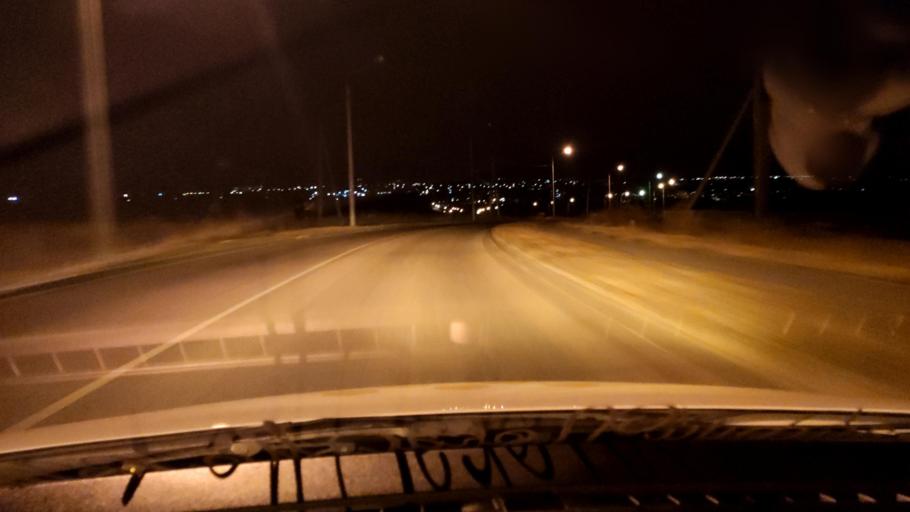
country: RU
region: Voronezj
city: Semiluki
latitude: 51.6666
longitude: 39.0379
